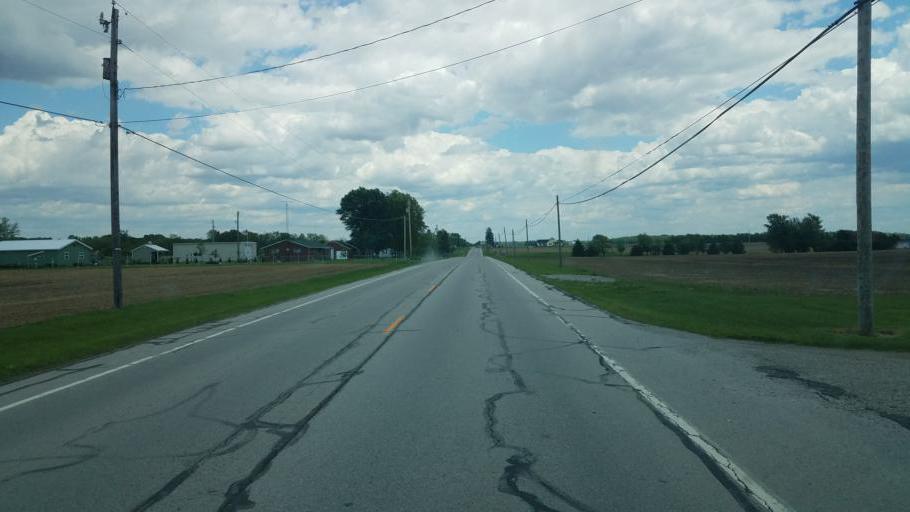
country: US
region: Ohio
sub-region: Crawford County
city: Bucyrus
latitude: 40.8128
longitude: -82.9101
